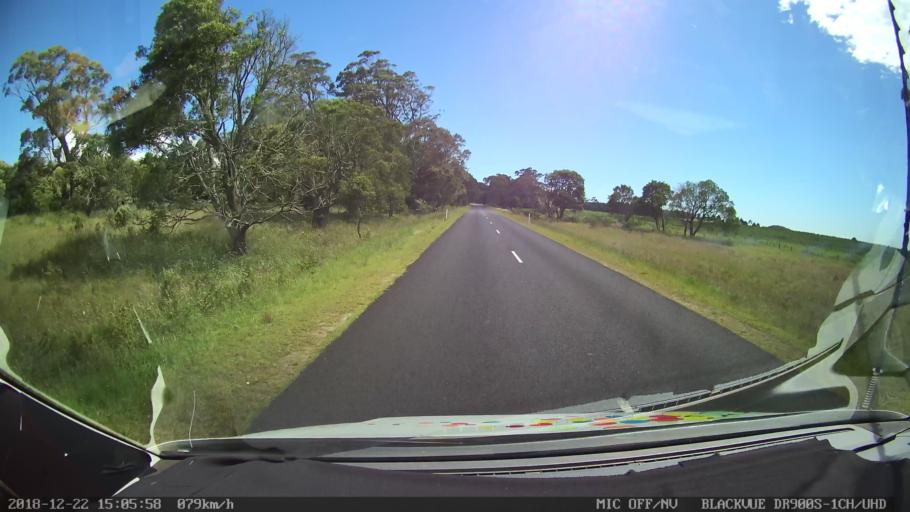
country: AU
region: New South Wales
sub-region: Bellingen
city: Dorrigo
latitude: -30.2891
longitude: 152.4314
